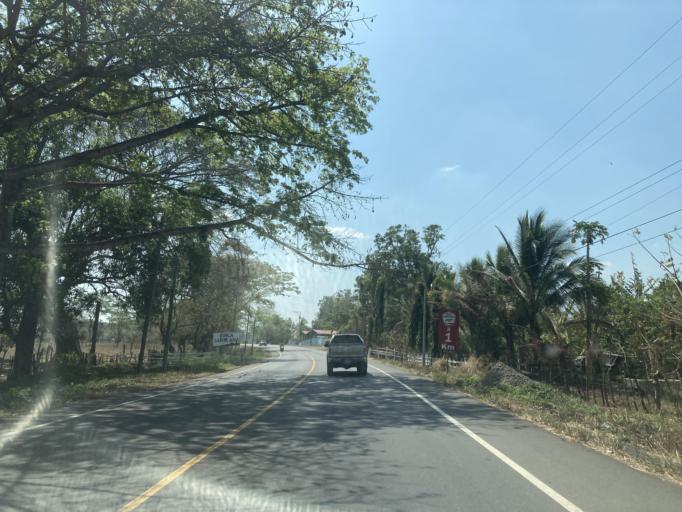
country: GT
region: Escuintla
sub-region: Municipio de Escuintla
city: Escuintla
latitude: 14.2386
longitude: -90.7420
